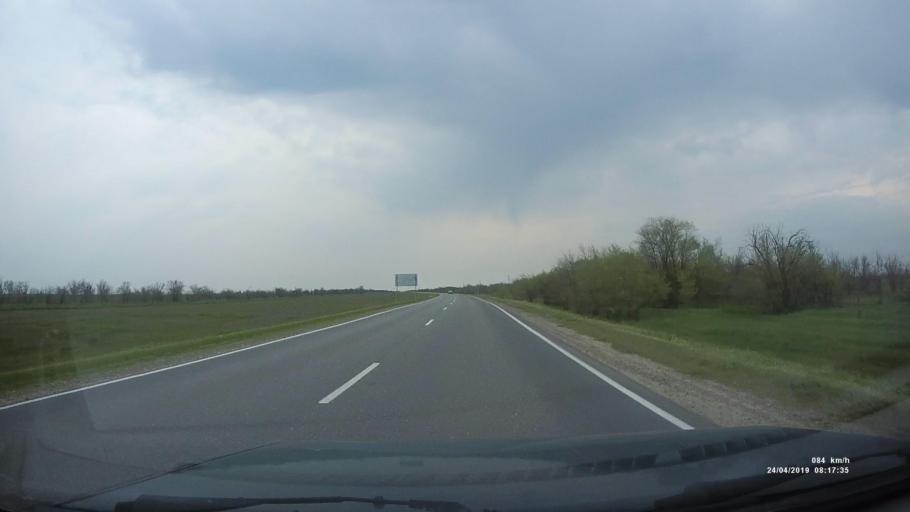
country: RU
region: Kalmykiya
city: Priyutnoye
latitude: 46.0968
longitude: 43.6327
